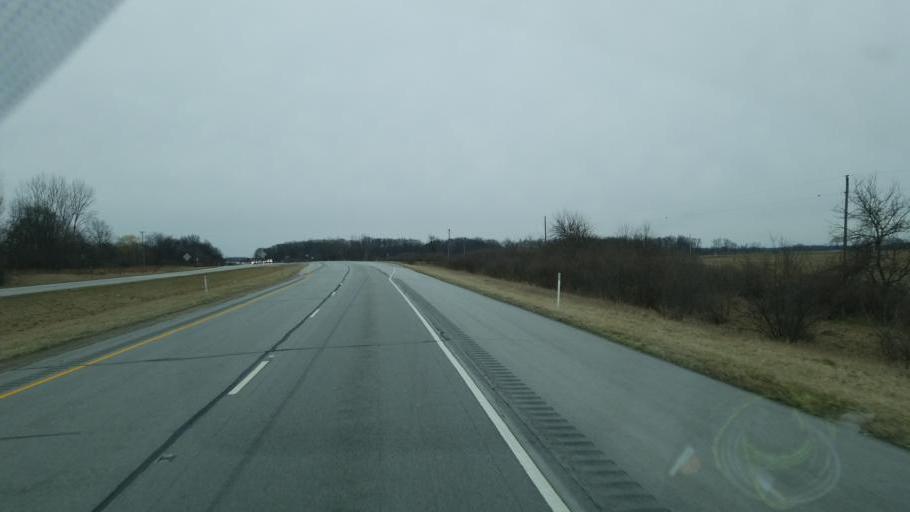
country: US
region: Indiana
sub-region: Marshall County
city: Argos
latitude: 41.2765
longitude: -86.2716
